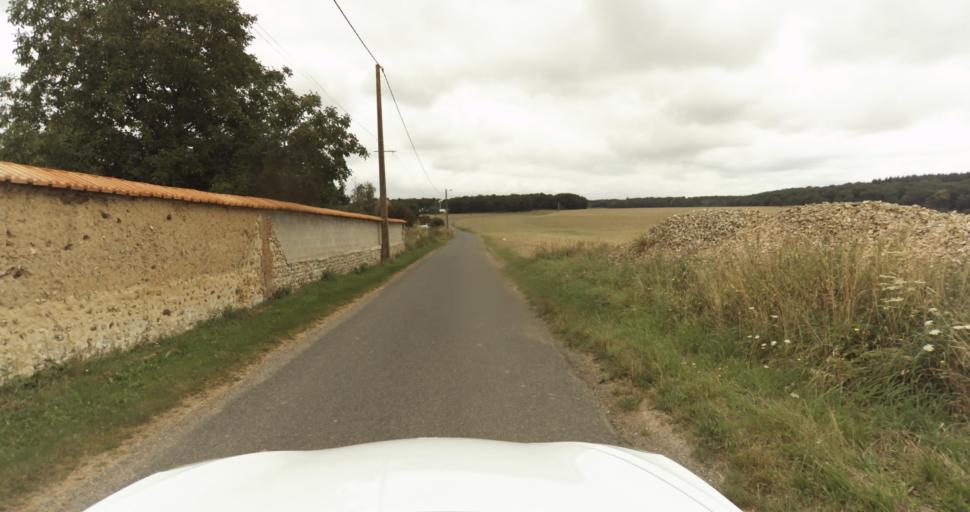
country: FR
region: Haute-Normandie
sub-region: Departement de l'Eure
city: Saint-Sebastien-de-Morsent
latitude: 49.0187
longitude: 1.0610
